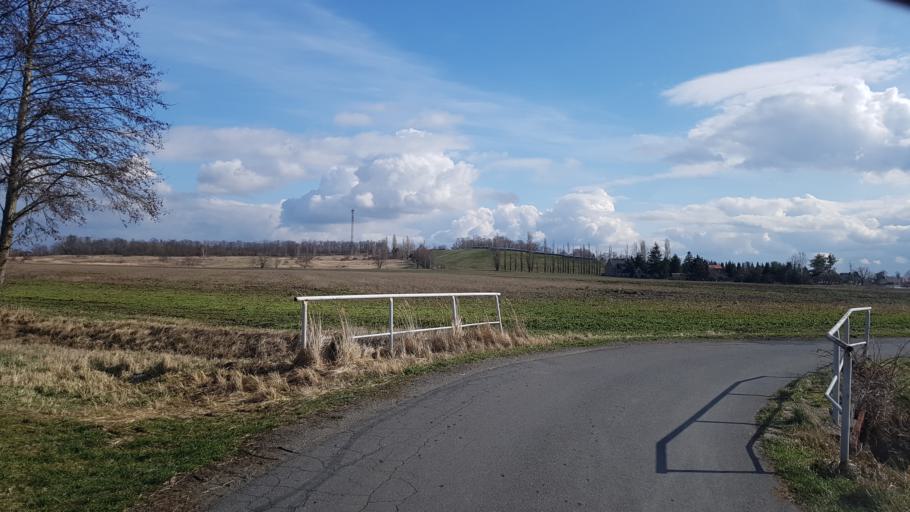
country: DE
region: Brandenburg
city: Elsterwerda
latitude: 51.4699
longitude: 13.5257
